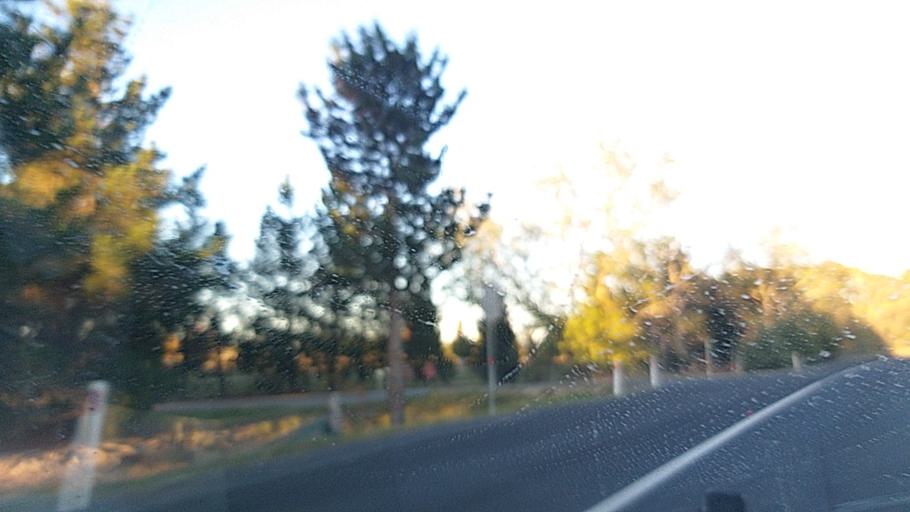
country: AU
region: New South Wales
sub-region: Goulburn Mulwaree
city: Goulburn
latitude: -34.8923
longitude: 149.5253
